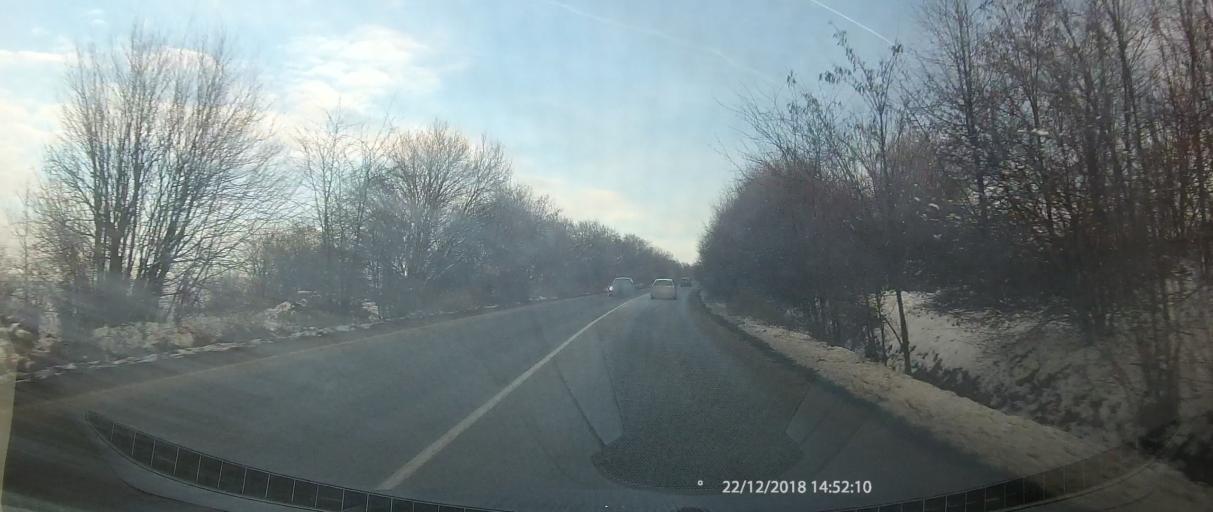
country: BG
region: Veliko Turnovo
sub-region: Obshtina Polski Trumbesh
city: Polski Trumbesh
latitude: 43.4305
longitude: 25.5049
